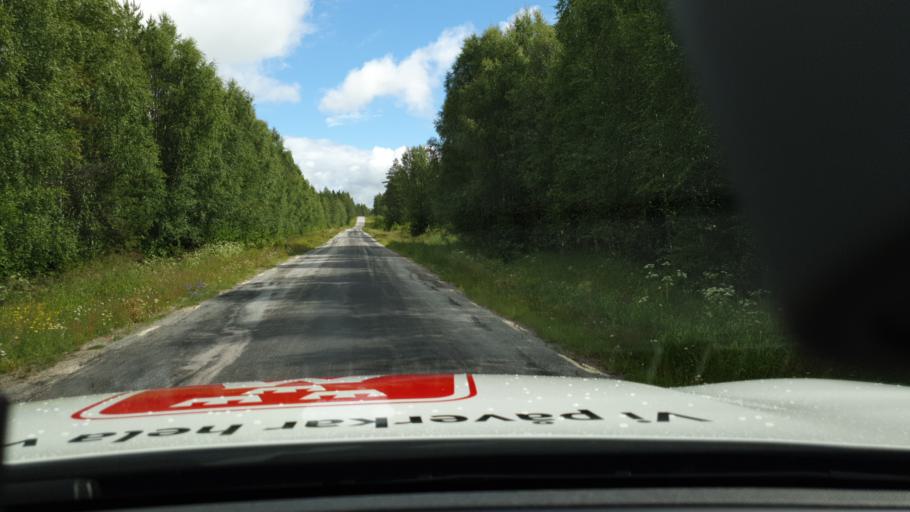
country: SE
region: Norrbotten
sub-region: Pitea Kommun
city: Rosvik
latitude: 65.4134
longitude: 21.7670
